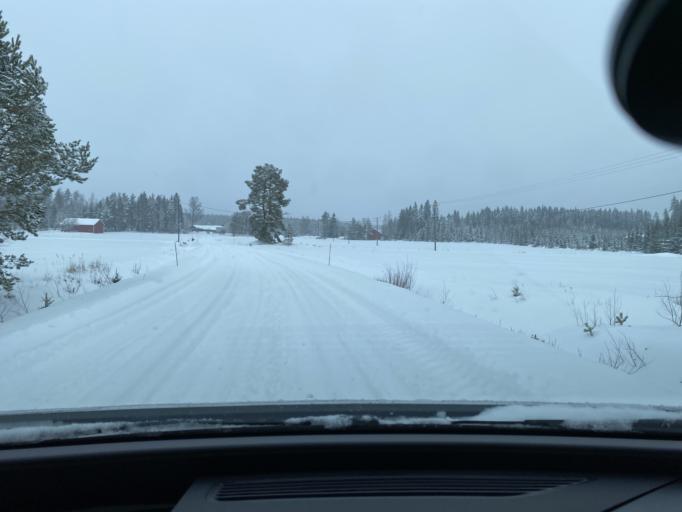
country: FI
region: Haeme
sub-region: Forssa
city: Humppila
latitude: 61.0100
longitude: 23.3027
